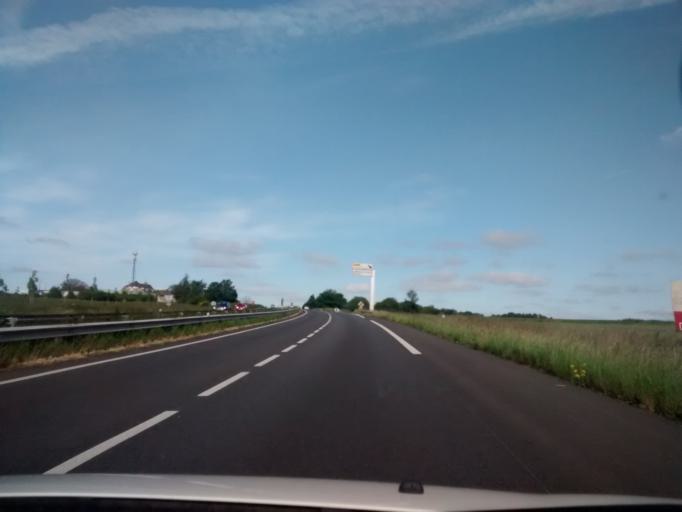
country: FR
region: Brittany
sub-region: Departement des Cotes-d'Armor
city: Lamballe
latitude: 48.4542
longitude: -2.4907
